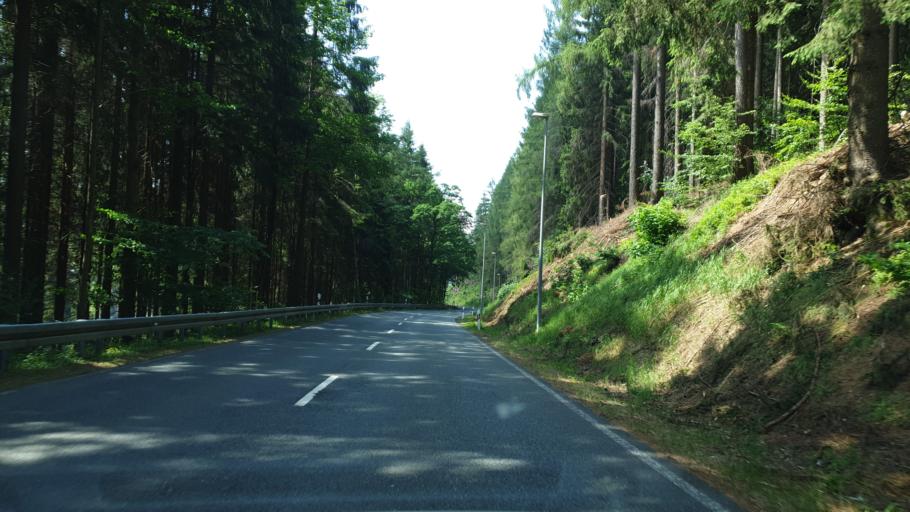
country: DE
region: Saxony
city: Klingenthal
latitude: 50.3875
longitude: 12.4916
